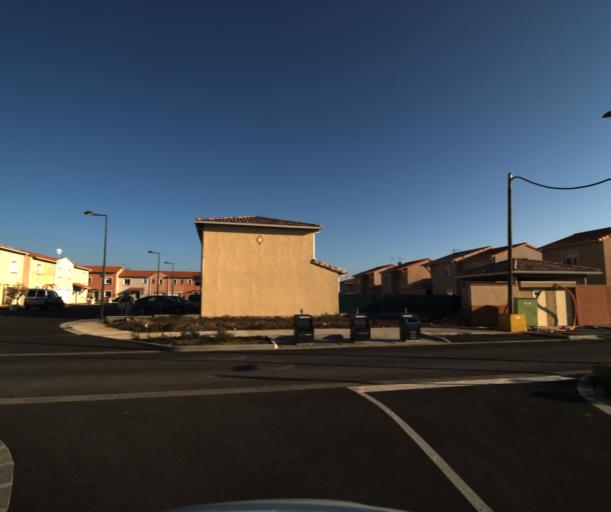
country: FR
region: Midi-Pyrenees
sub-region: Departement de la Haute-Garonne
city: Colomiers
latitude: 43.6245
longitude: 1.3231
